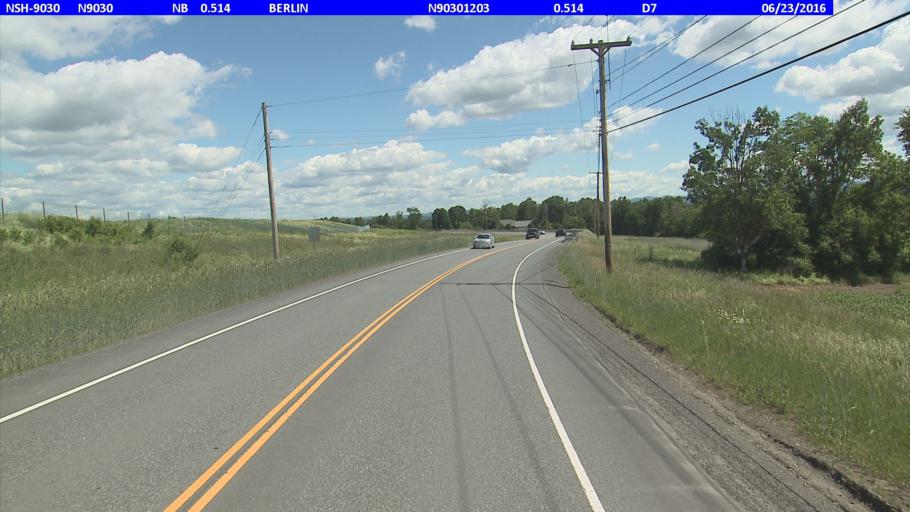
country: US
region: Vermont
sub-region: Washington County
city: Montpelier
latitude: 44.2098
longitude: -72.5574
